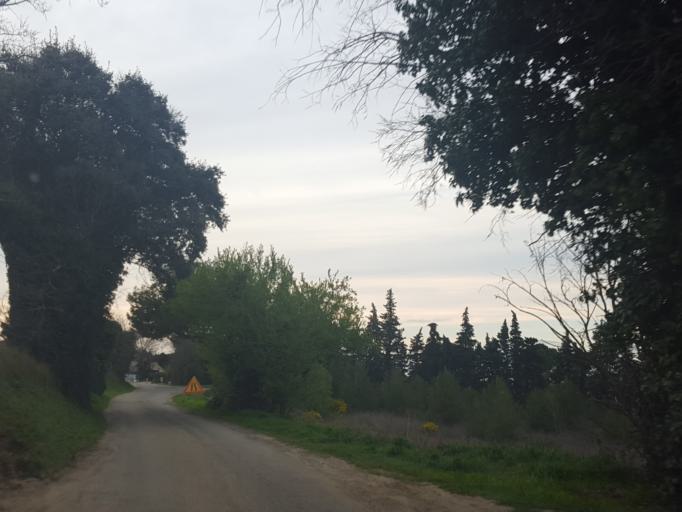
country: FR
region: Provence-Alpes-Cote d'Azur
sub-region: Departement du Vaucluse
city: Jonquerettes
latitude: 43.9447
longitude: 4.9382
